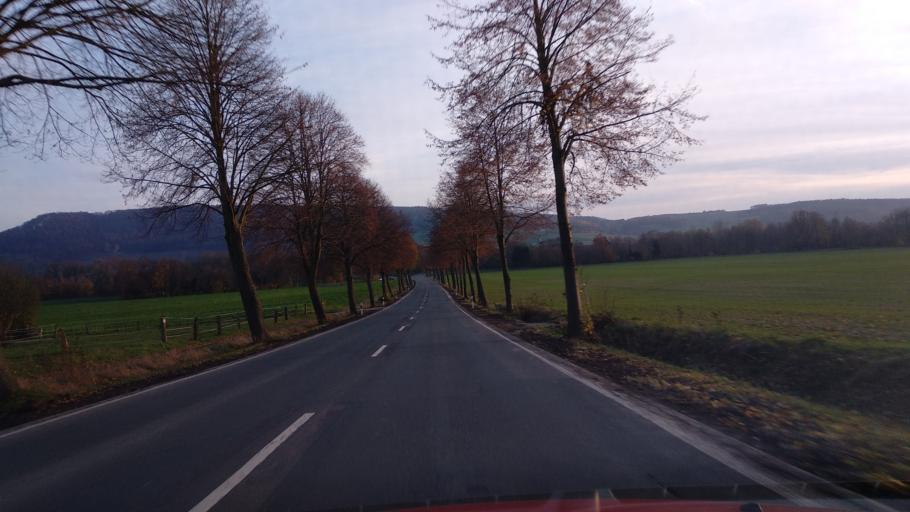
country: DE
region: Lower Saxony
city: Boffzen
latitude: 51.7199
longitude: 9.3402
